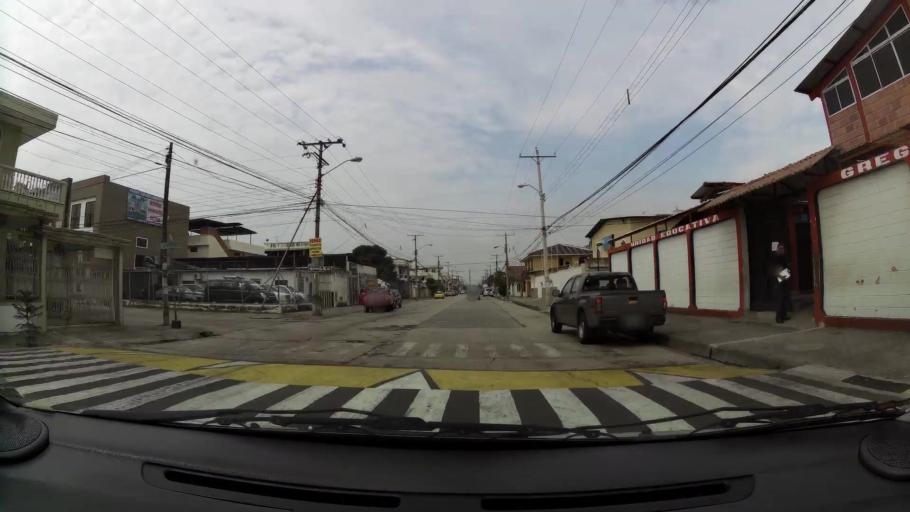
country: EC
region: Guayas
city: Eloy Alfaro
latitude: -2.1479
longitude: -79.8972
